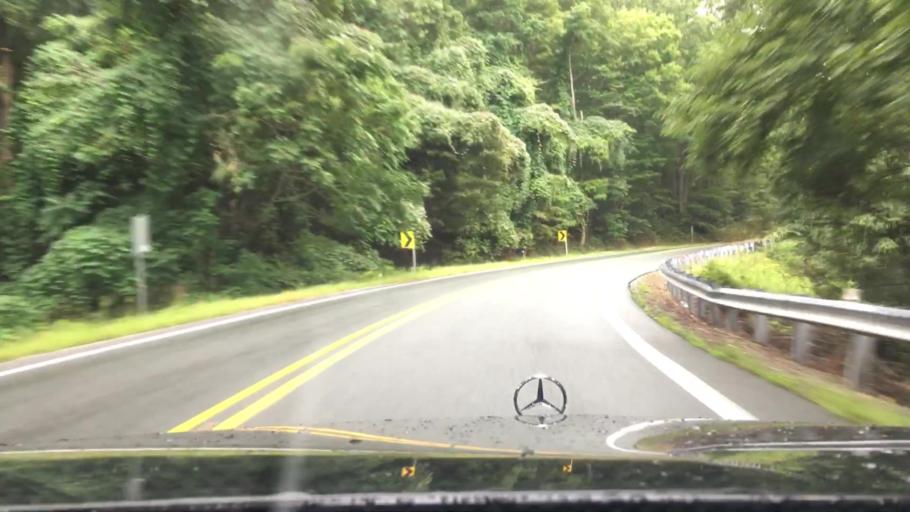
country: US
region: Virginia
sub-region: Nelson County
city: Nellysford
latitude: 37.8610
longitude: -78.9201
